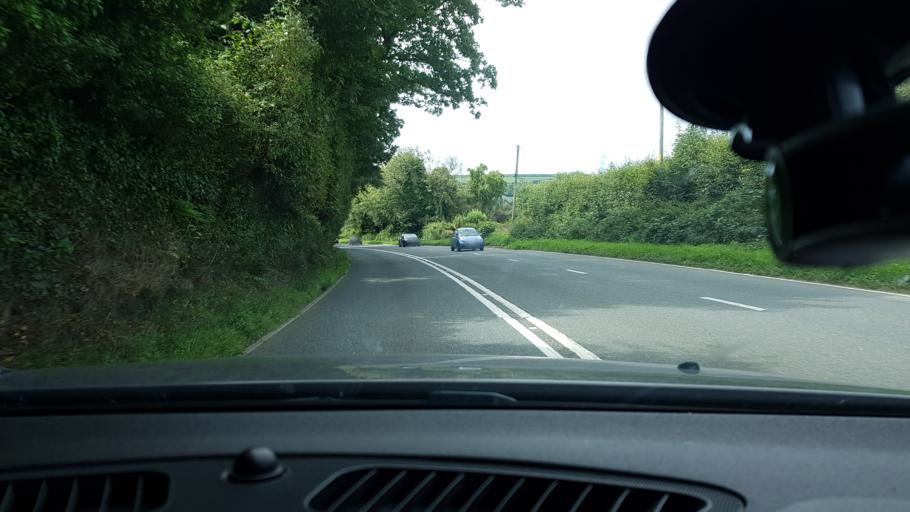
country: GB
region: England
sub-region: Cornwall
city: Camelford
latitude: 50.5950
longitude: -4.7195
